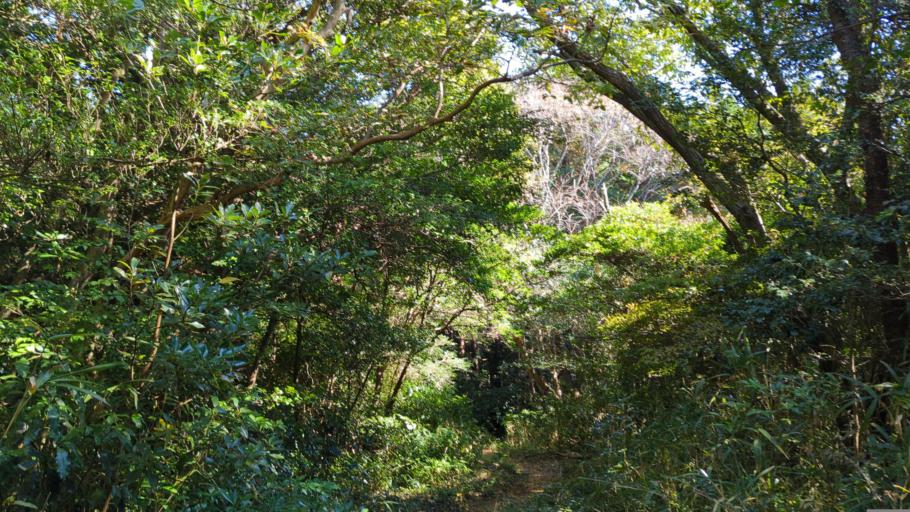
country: JP
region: Aichi
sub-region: Tokai-shi
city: Toyokawa
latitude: 34.7718
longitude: 137.4560
